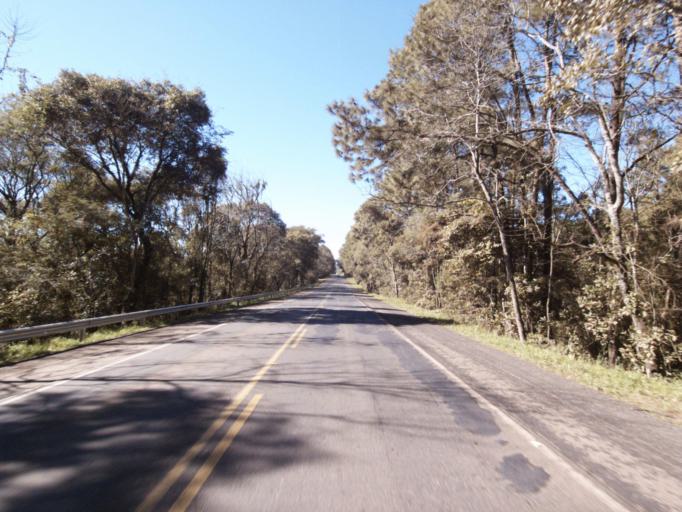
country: BR
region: Santa Catarina
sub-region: Sao Lourenco Do Oeste
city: Sao Lourenco dOeste
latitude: -26.8254
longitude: -53.0679
